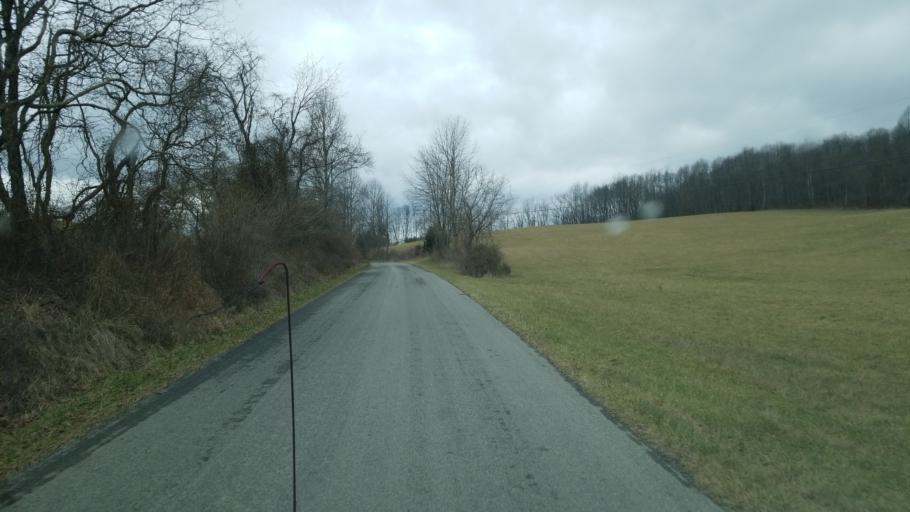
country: US
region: Virginia
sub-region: Giles County
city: Pembroke
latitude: 37.2376
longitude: -80.6803
